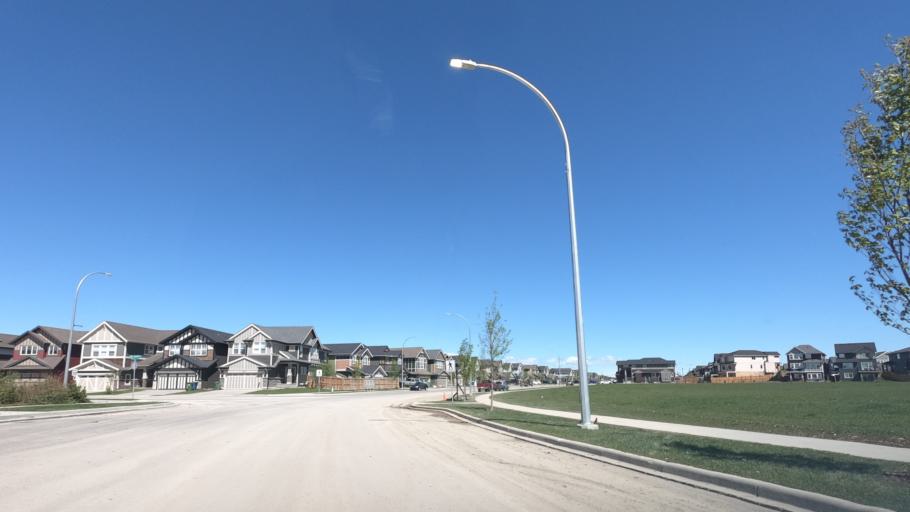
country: CA
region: Alberta
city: Airdrie
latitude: 51.2594
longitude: -113.9843
